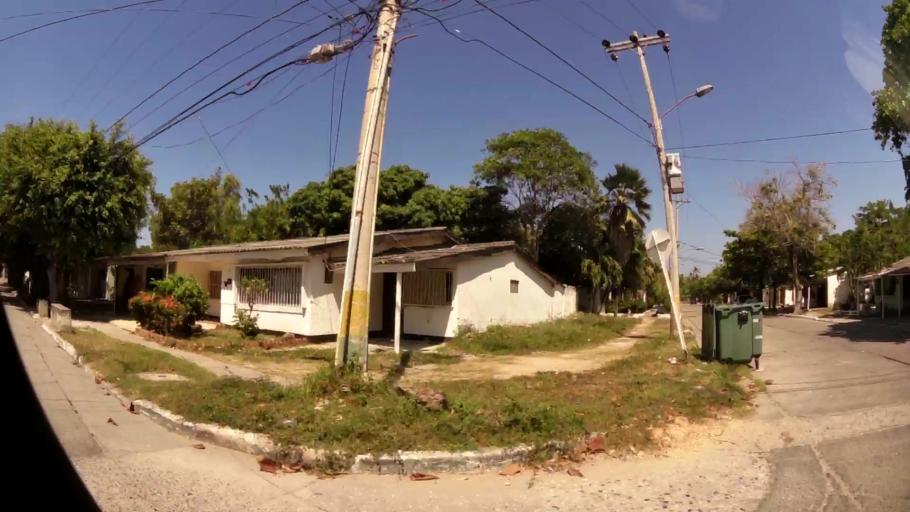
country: CO
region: Bolivar
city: Cartagena
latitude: 10.4482
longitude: -75.5149
